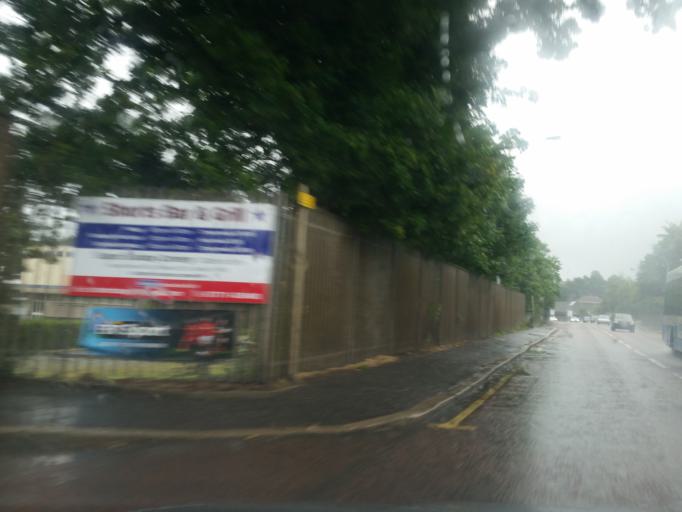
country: GB
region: Northern Ireland
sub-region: Castlereagh District
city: Castlereagh
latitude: 54.6122
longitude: -5.8639
